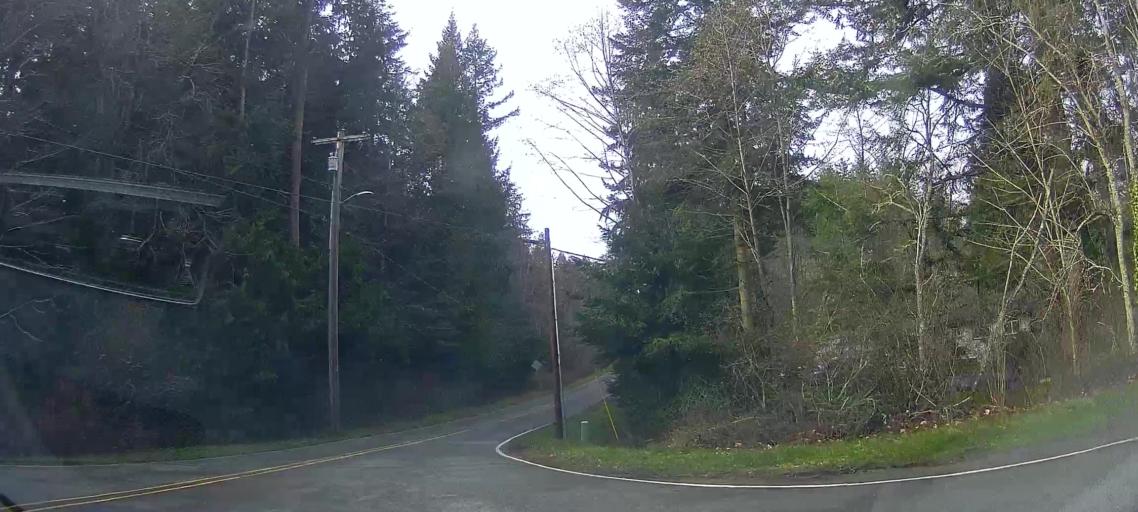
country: US
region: Washington
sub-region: Island County
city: Camano
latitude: 48.1974
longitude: -122.5273
